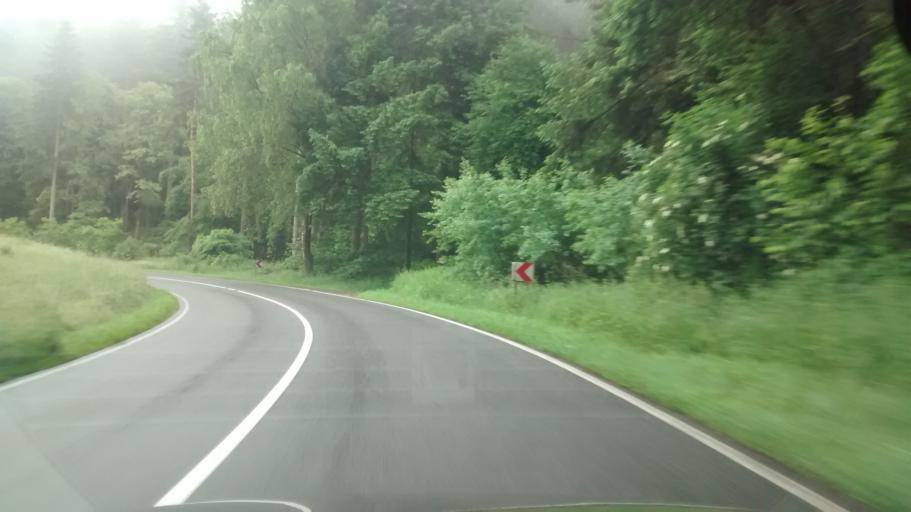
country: DE
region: Rheinland-Pfalz
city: Schindhard
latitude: 49.1371
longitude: 7.8088
